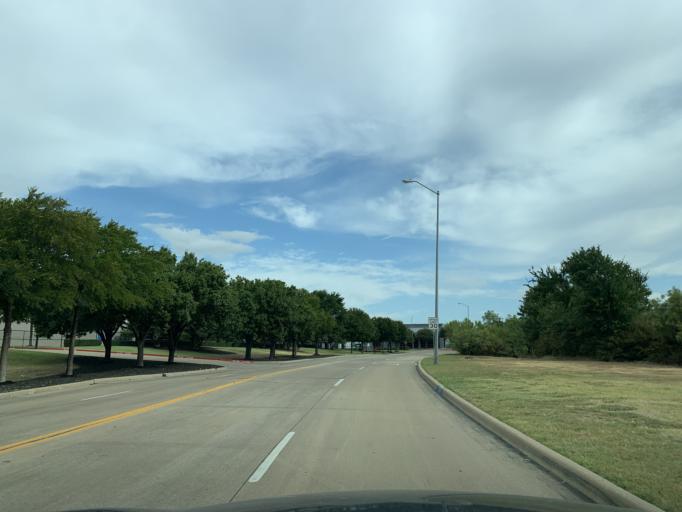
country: US
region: Texas
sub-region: Dallas County
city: Cockrell Hill
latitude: 32.7583
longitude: -96.8799
